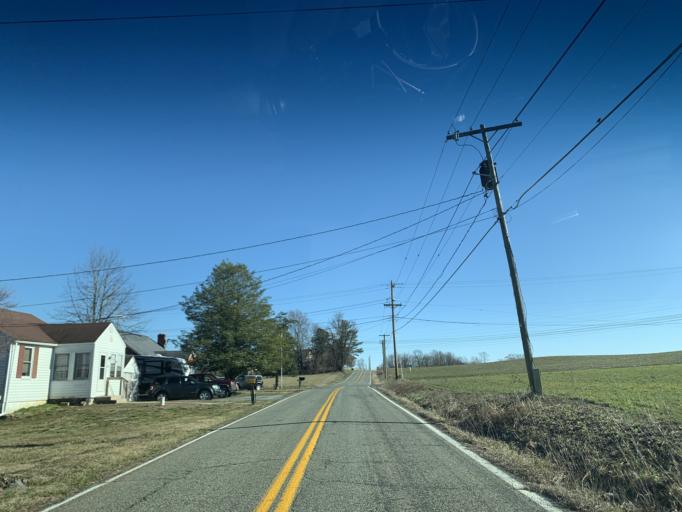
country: US
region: Maryland
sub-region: Cecil County
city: Rising Sun
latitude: 39.6824
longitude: -76.1009
